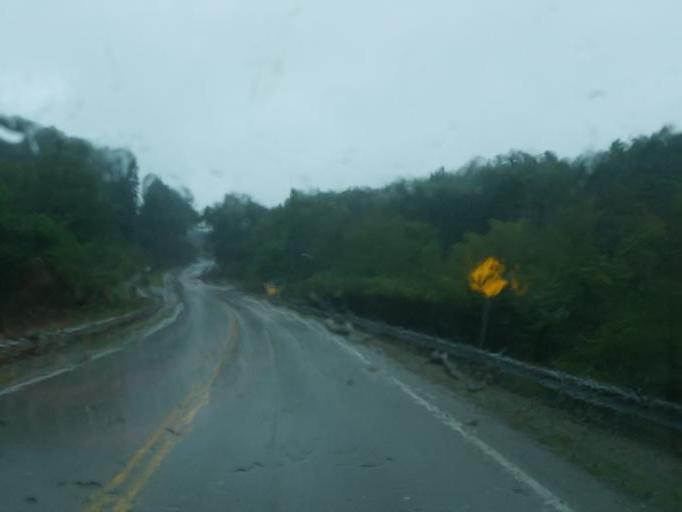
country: US
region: Kentucky
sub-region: Carter County
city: Olive Hill
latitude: 38.3358
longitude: -83.2028
